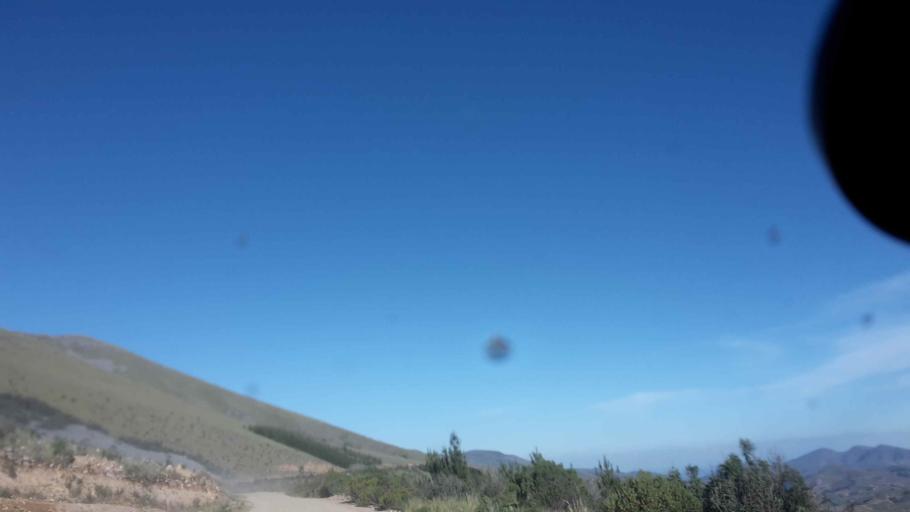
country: BO
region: Cochabamba
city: Arani
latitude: -17.7178
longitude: -65.6639
